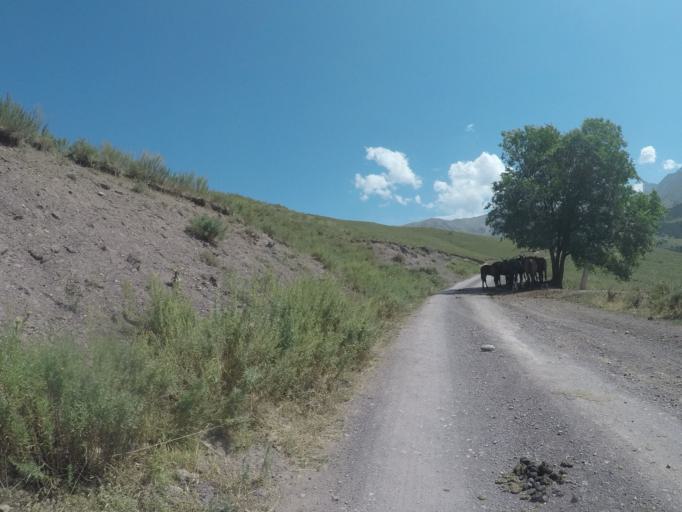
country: KG
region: Chuy
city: Bishkek
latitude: 42.6509
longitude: 74.5198
